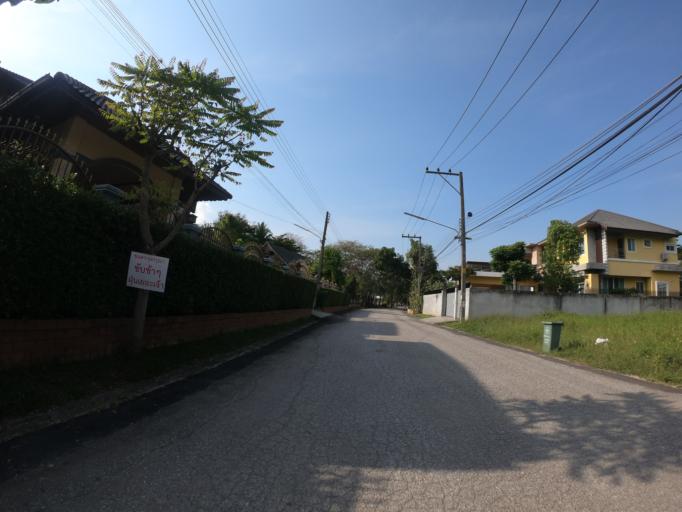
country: TH
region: Chiang Mai
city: San Sai
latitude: 18.8339
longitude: 99.0067
